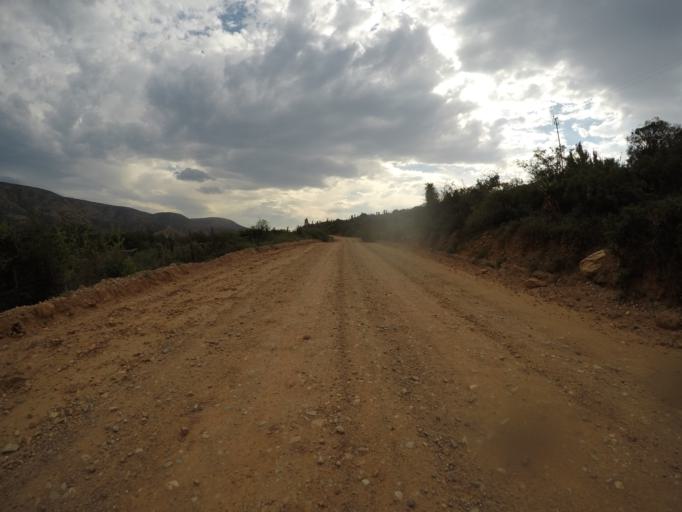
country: ZA
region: Eastern Cape
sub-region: Cacadu District Municipality
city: Kareedouw
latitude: -33.5877
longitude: 24.1698
